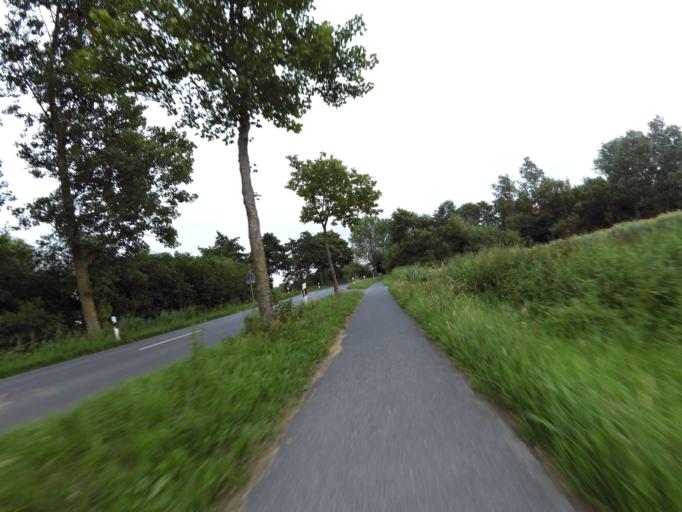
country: DE
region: Lower Saxony
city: Dorum
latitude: 53.6990
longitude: 8.5604
